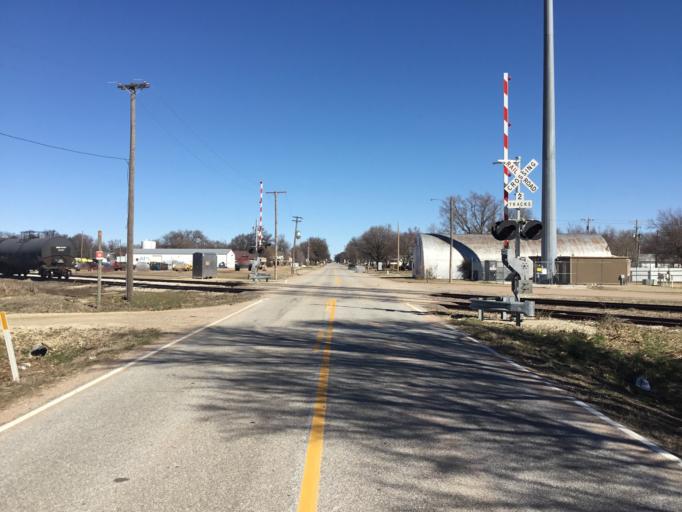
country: US
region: Kansas
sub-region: Reno County
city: Haven
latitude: 37.8628
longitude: -97.6653
